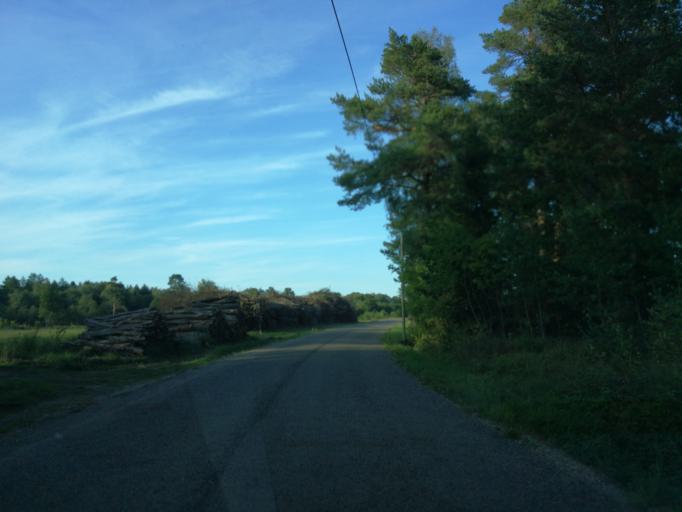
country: LV
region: Garkalne
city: Garkalne
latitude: 57.0781
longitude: 24.4599
